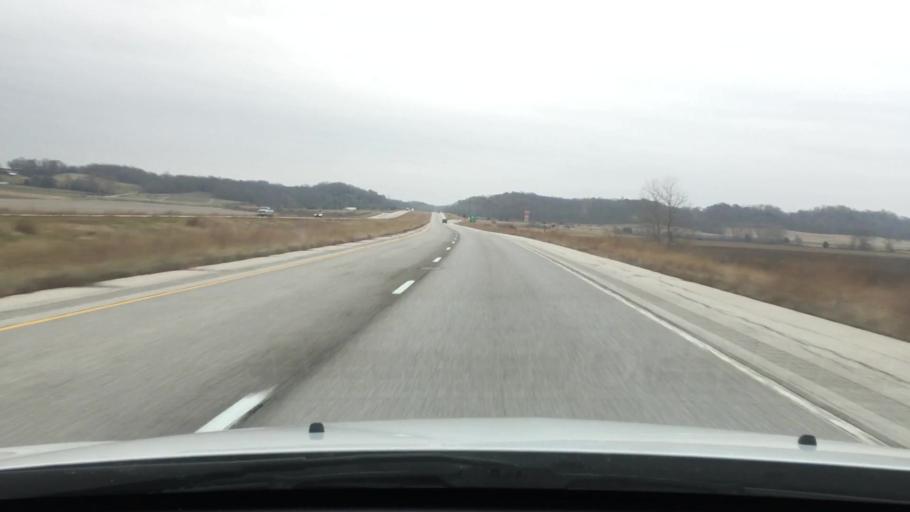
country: US
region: Illinois
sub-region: Scott County
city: Winchester
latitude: 39.6850
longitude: -90.5839
